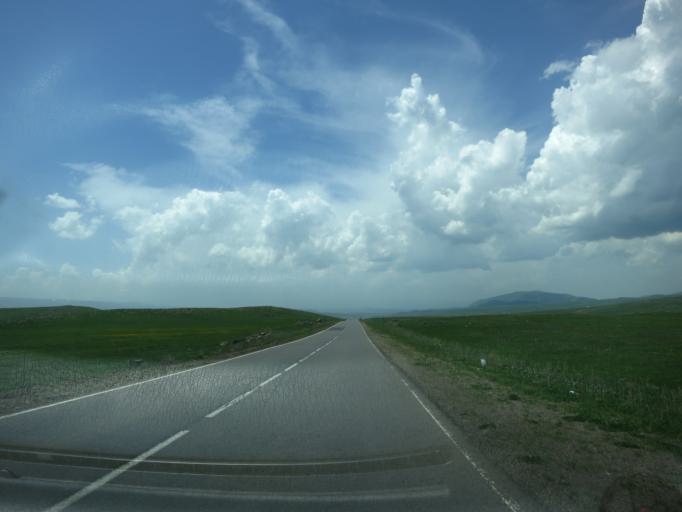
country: GE
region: Samtskhe-Javakheti
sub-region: Ninotsminda
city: Ninotsminda
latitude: 41.2915
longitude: 43.7160
